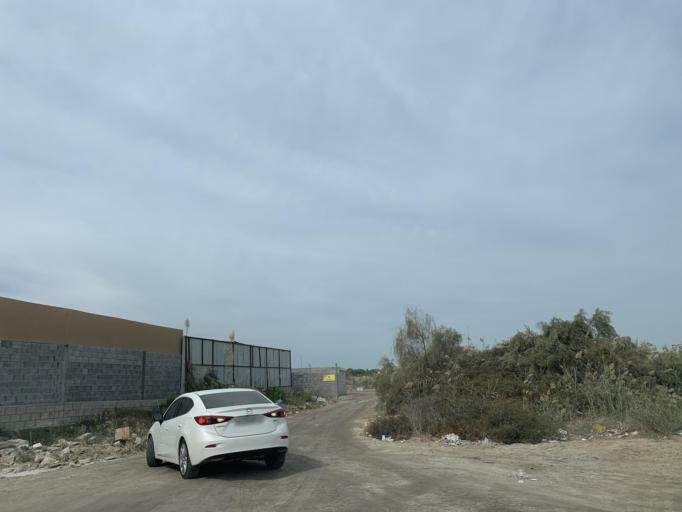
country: BH
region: Central Governorate
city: Madinat Hamad
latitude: 26.1100
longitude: 50.4768
